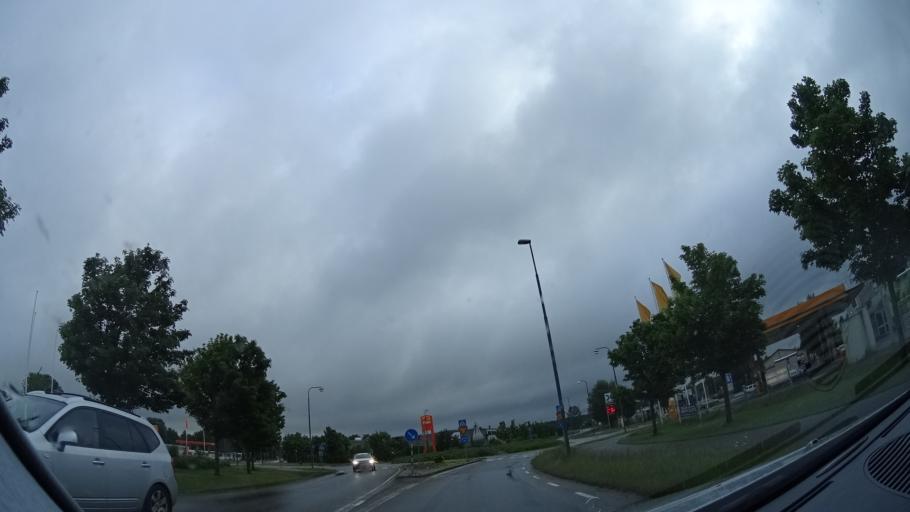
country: SE
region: Skane
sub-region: Hoors Kommun
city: Hoeoer
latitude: 55.9260
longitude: 13.5444
